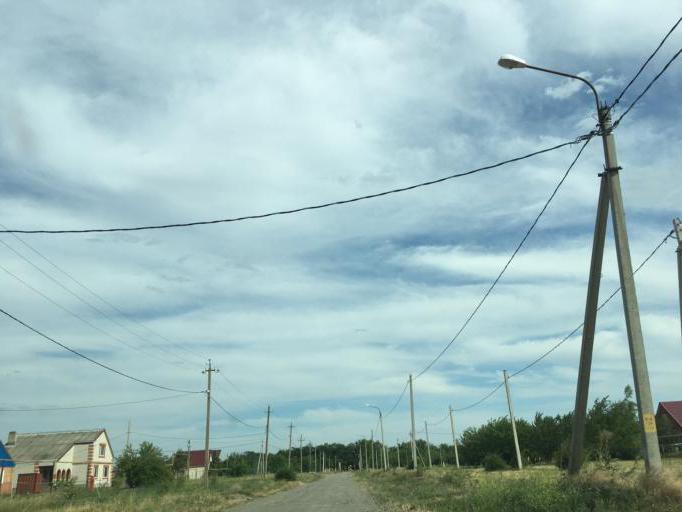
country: RU
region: Krasnodarskiy
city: Kushchevskaya
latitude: 46.5509
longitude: 39.6702
